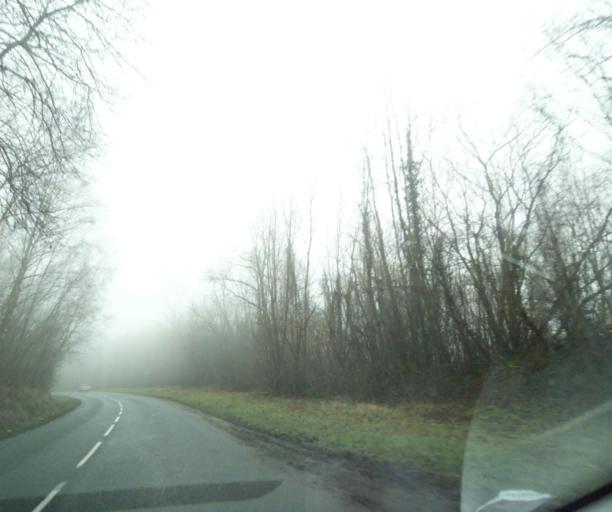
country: FR
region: Ile-de-France
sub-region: Departement de Seine-et-Marne
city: Saint-Mard
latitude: 49.0471
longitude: 2.6891
